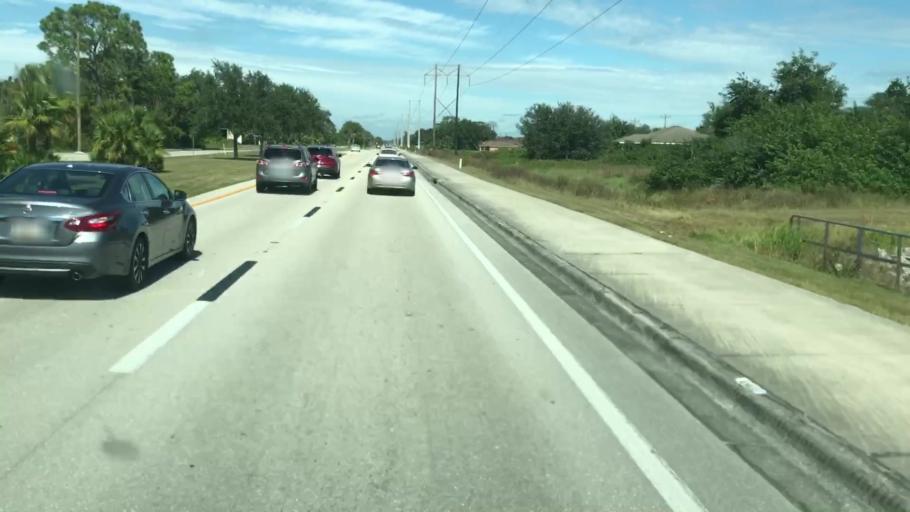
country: US
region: Florida
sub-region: Lee County
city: Gateway
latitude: 26.5988
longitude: -81.7129
